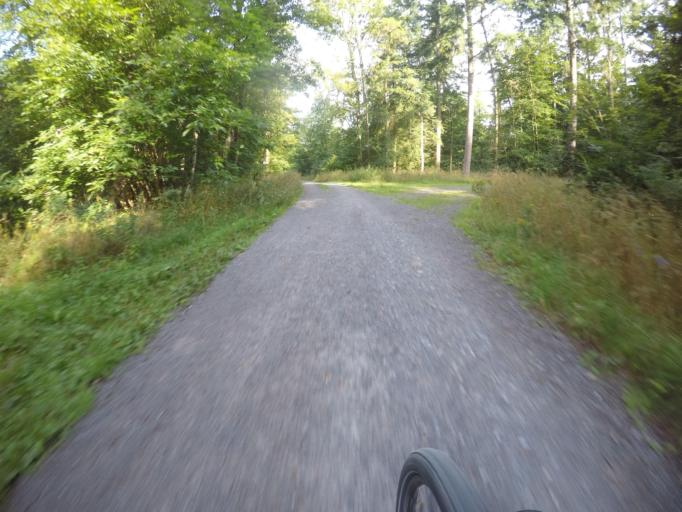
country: DE
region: Baden-Wuerttemberg
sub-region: Regierungsbezirk Stuttgart
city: Rutesheim
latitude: 48.8356
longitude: 8.9563
